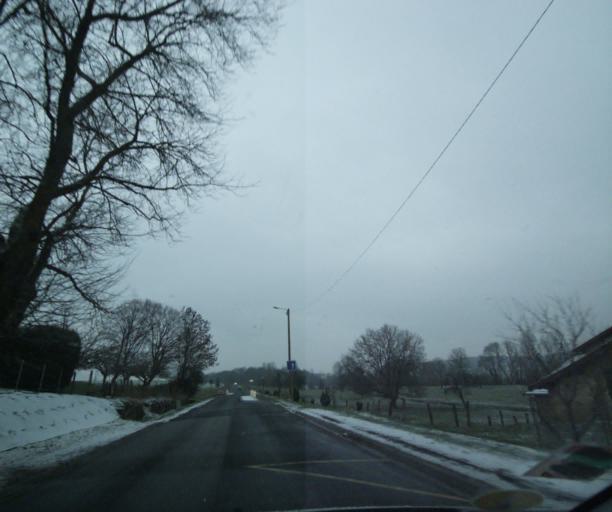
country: FR
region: Champagne-Ardenne
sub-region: Departement de la Haute-Marne
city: Wassy
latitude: 48.4469
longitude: 4.9568
